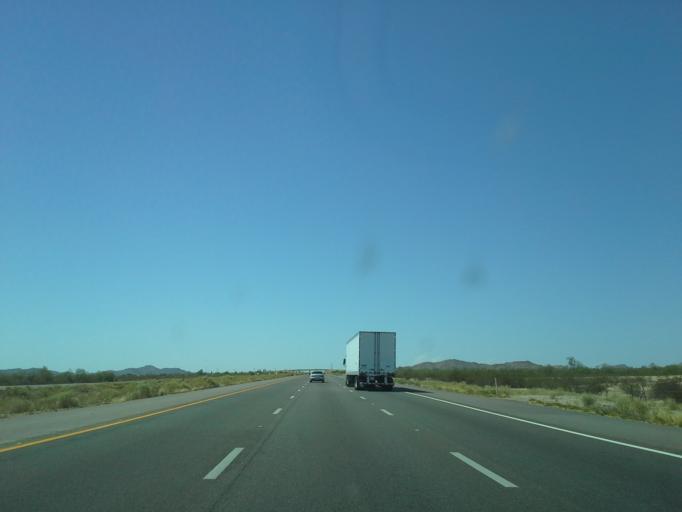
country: US
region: Arizona
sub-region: Pinal County
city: Casa Grande
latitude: 32.9563
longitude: -111.7152
